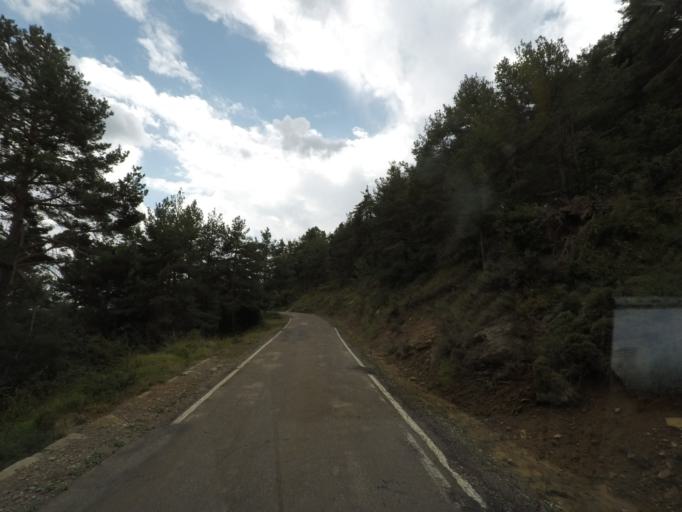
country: ES
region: Aragon
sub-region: Provincia de Huesca
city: Boltana
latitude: 42.4041
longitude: -0.0299
